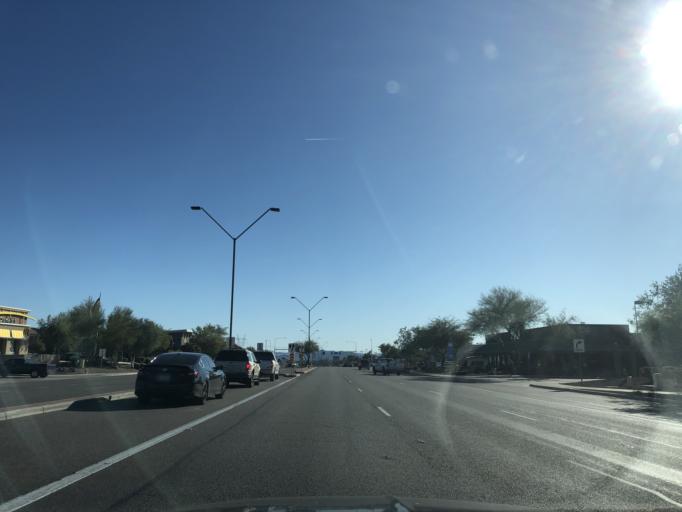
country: US
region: Arizona
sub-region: Maricopa County
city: Buckeye
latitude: 33.4423
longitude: -112.5565
